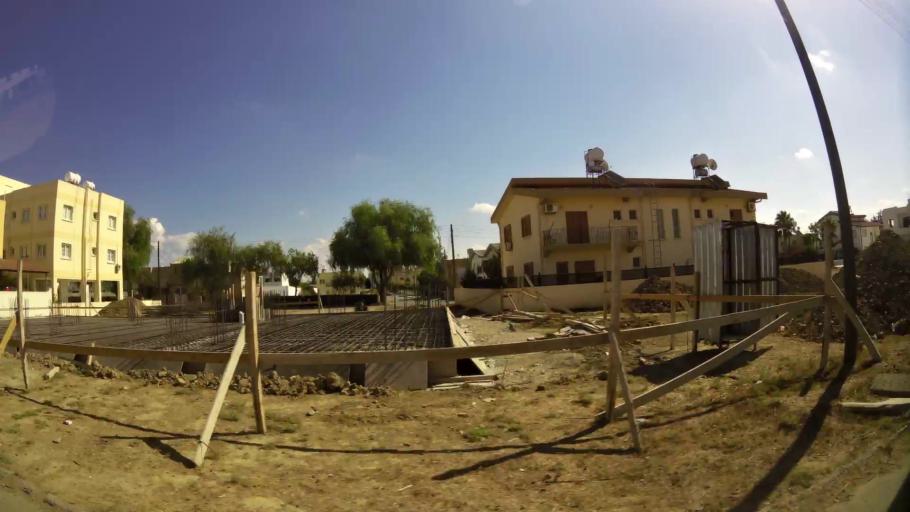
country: CY
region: Lefkosia
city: Nicosia
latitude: 35.2093
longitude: 33.3321
